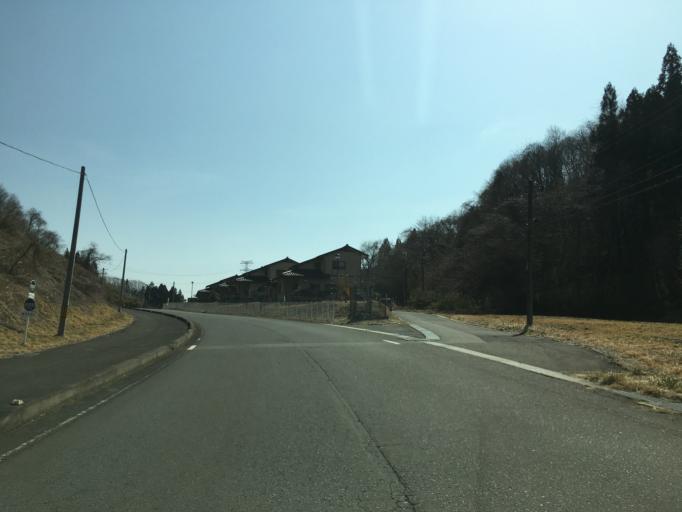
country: JP
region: Fukushima
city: Ishikawa
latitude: 37.0399
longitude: 140.4719
